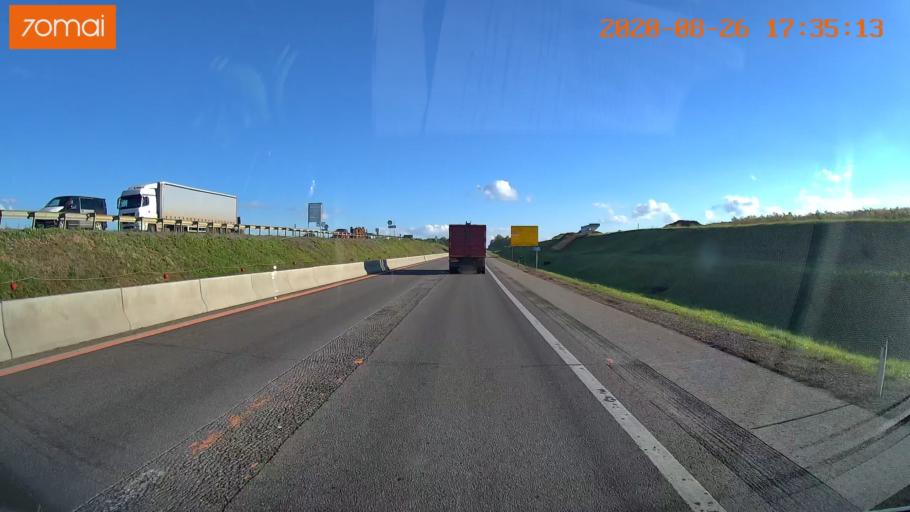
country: RU
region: Tula
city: Kazachka
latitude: 53.3860
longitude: 38.1847
